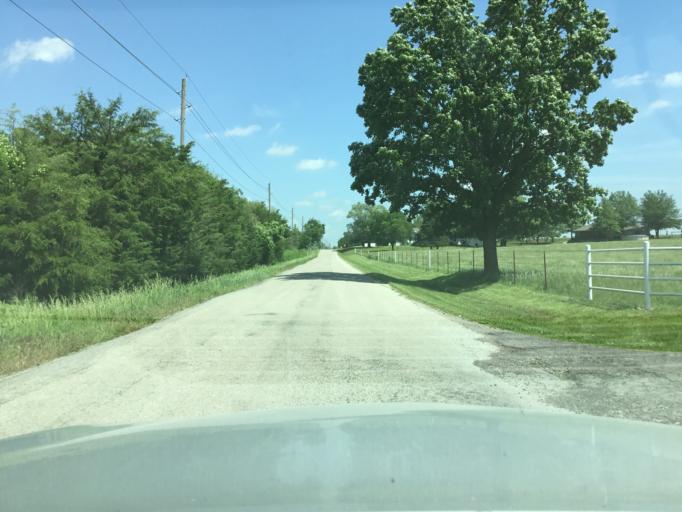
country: US
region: Kansas
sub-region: Labette County
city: Parsons
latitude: 37.3530
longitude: -95.2495
